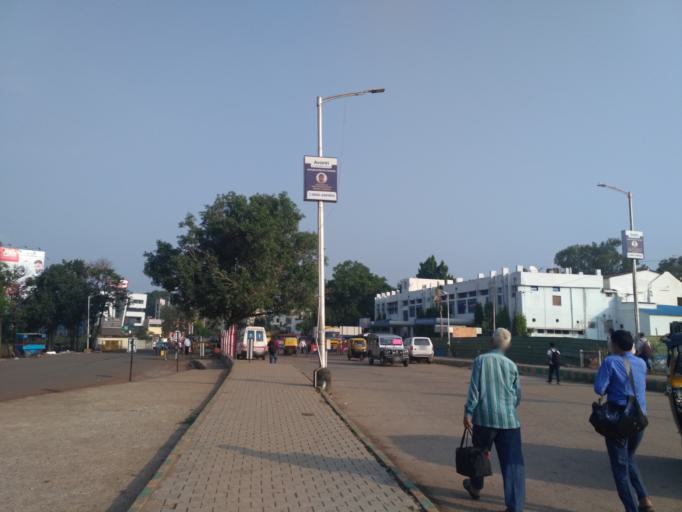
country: IN
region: Karnataka
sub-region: Dharwad
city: Hubli
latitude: 15.3510
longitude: 75.1476
